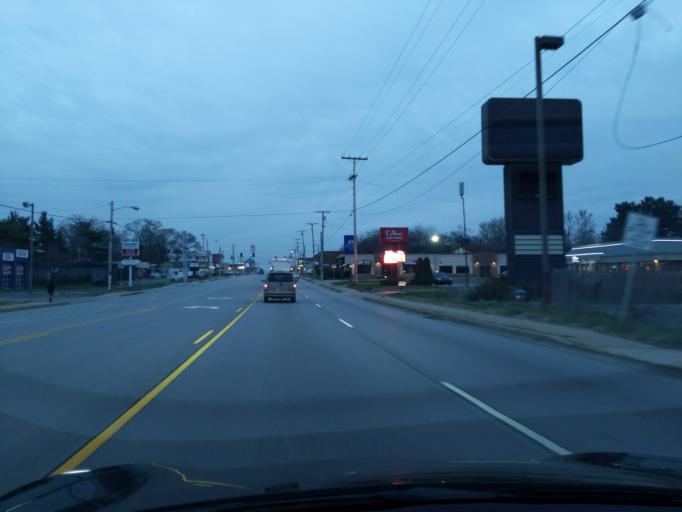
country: US
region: Indiana
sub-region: Saint Joseph County
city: Notre Dame
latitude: 41.7204
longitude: -86.2502
